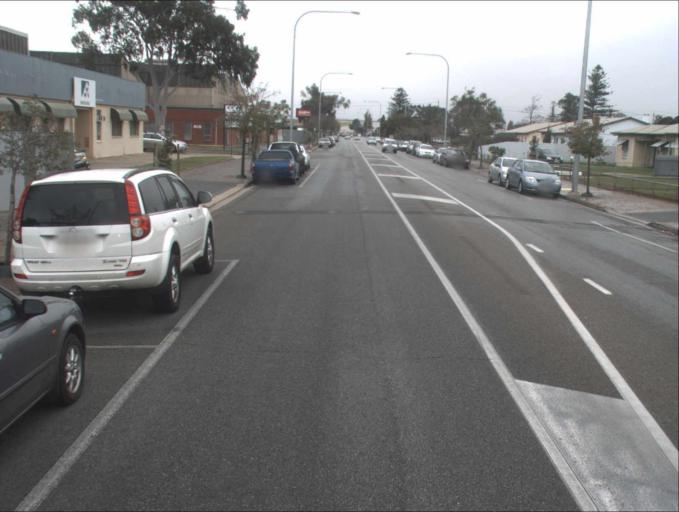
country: AU
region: South Australia
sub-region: Port Adelaide Enfield
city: Blair Athol
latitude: -34.8525
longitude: 138.5916
